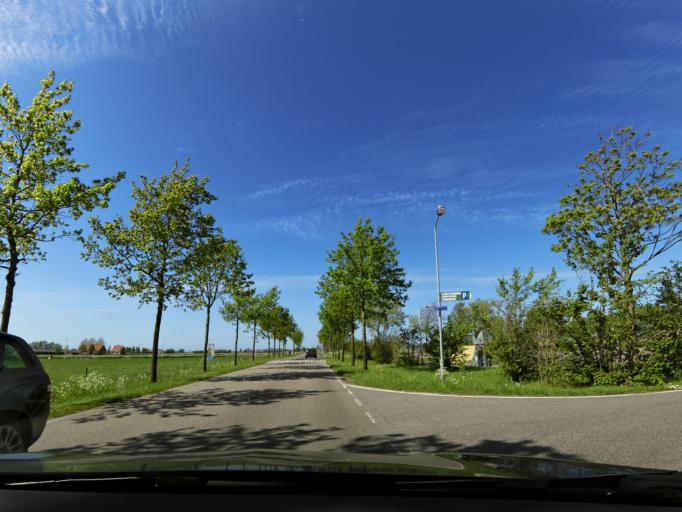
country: NL
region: Zeeland
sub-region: Schouwen-Duiveland
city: Bruinisse
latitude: 51.6498
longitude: 3.9957
